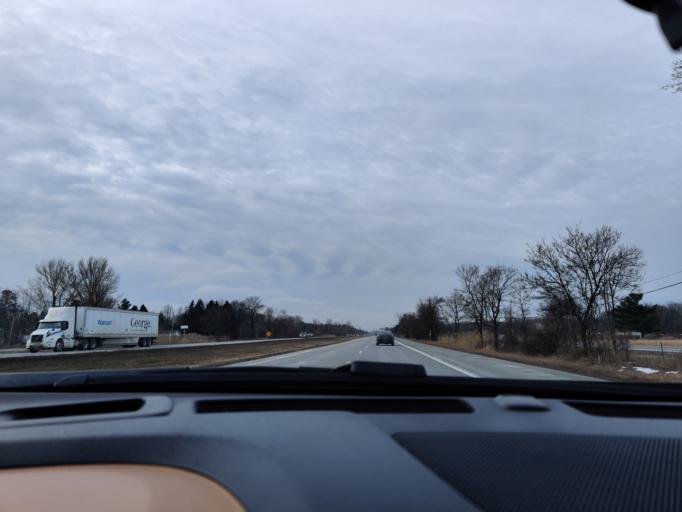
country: CA
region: Quebec
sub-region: Monteregie
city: Les Coteaux
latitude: 45.1598
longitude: -74.4519
